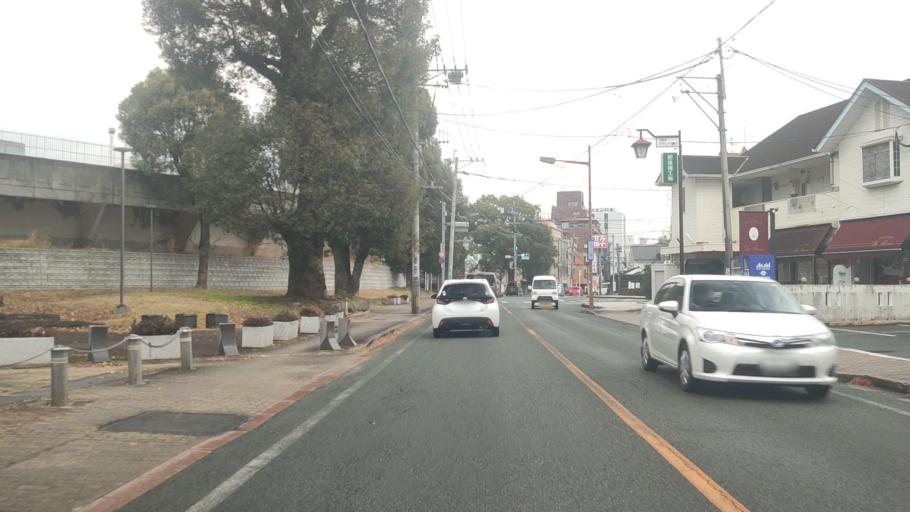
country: JP
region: Kumamoto
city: Kumamoto
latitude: 32.7930
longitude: 130.7405
